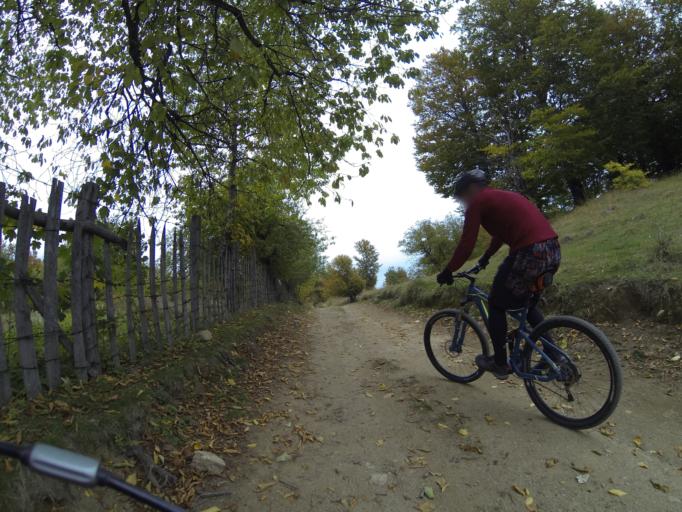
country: RO
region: Gorj
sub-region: Comuna Pades
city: Closani
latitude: 45.0955
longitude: 22.8384
